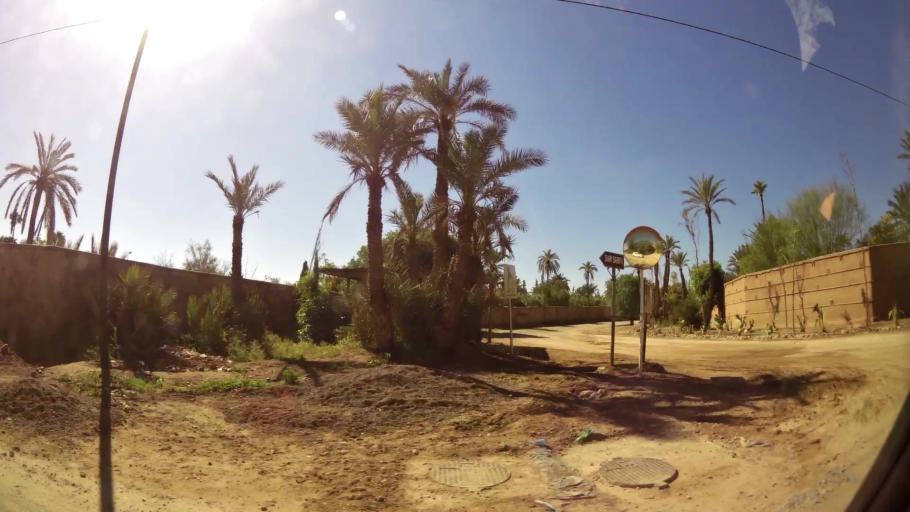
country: MA
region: Marrakech-Tensift-Al Haouz
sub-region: Marrakech
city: Marrakesh
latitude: 31.6706
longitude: -7.9600
